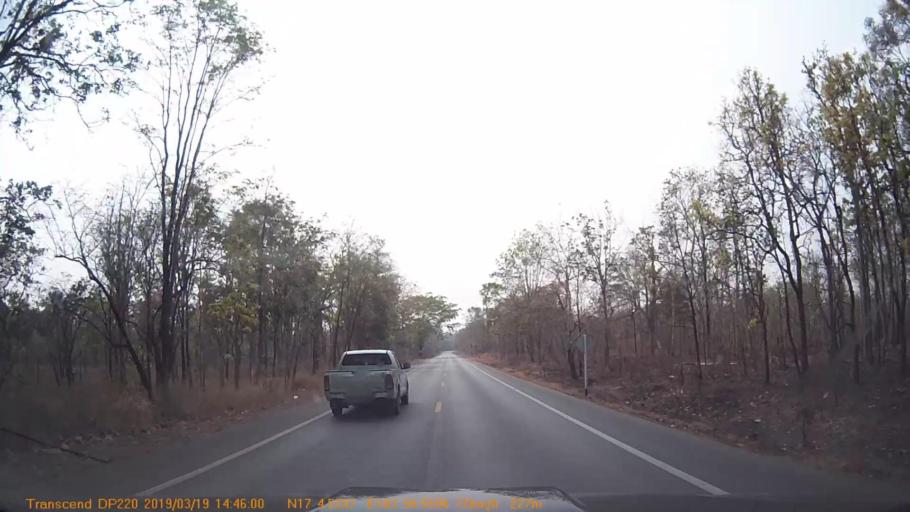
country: TH
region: Sakon Nakhon
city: Phu Phan
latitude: 17.0756
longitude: 103.9424
